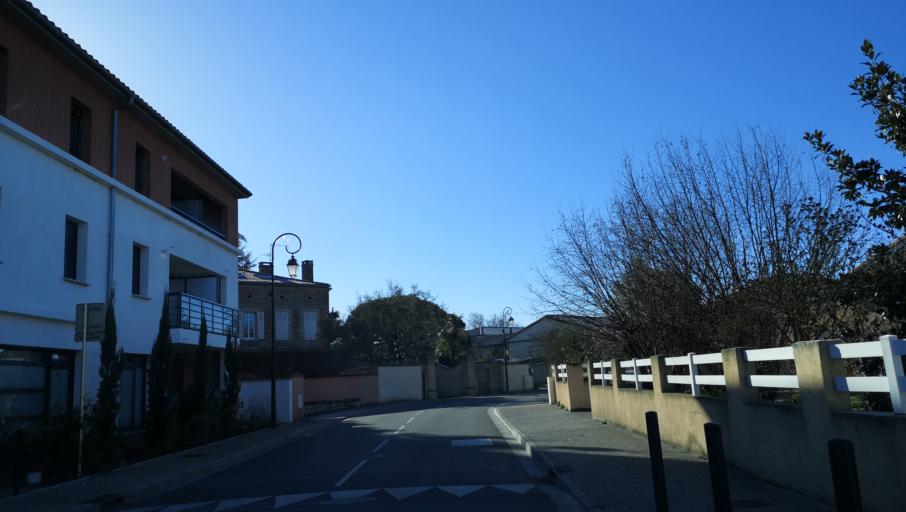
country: FR
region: Midi-Pyrenees
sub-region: Departement de la Haute-Garonne
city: Beauzelle
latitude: 43.6661
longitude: 1.3779
